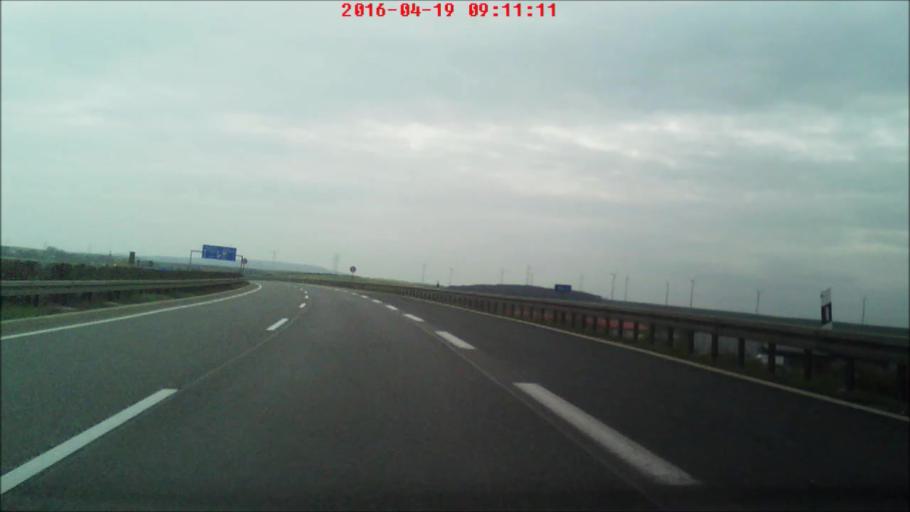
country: DE
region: Thuringia
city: Noda
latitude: 51.0389
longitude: 11.0358
